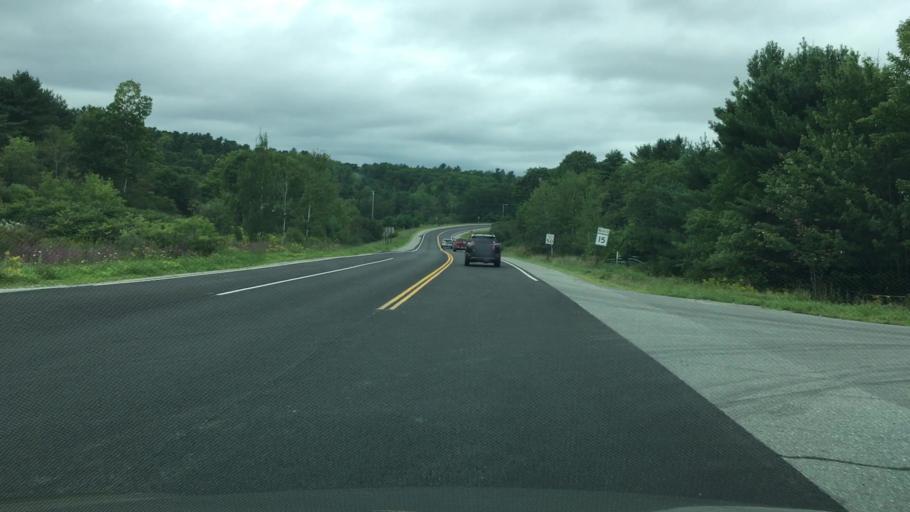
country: US
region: Maine
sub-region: Penobscot County
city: Orrington
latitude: 44.6958
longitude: -68.8158
